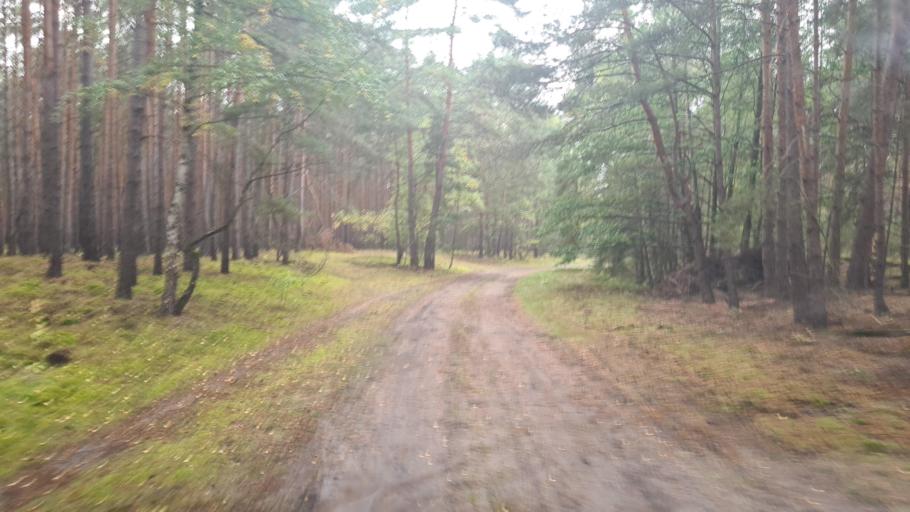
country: DE
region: Brandenburg
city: Storkow
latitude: 52.2243
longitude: 13.9135
